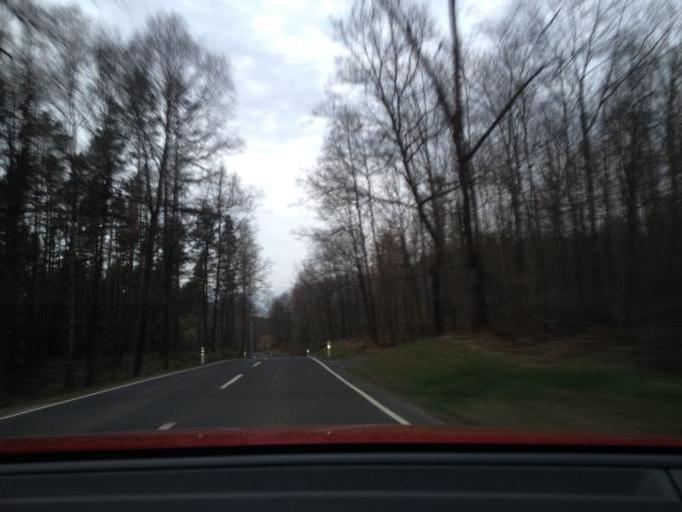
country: DE
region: Bavaria
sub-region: Upper Palatinate
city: Speinshart
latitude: 49.8019
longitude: 11.8205
